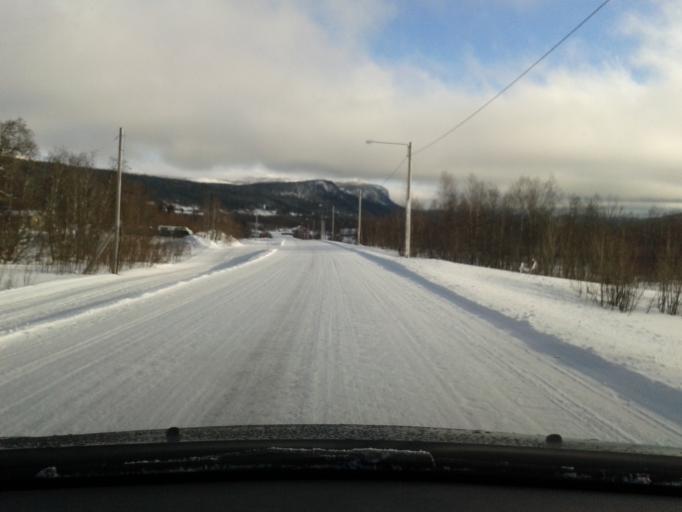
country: SE
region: Vaesterbotten
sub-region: Vilhelmina Kommun
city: Sjoberg
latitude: 65.2499
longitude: 15.4948
